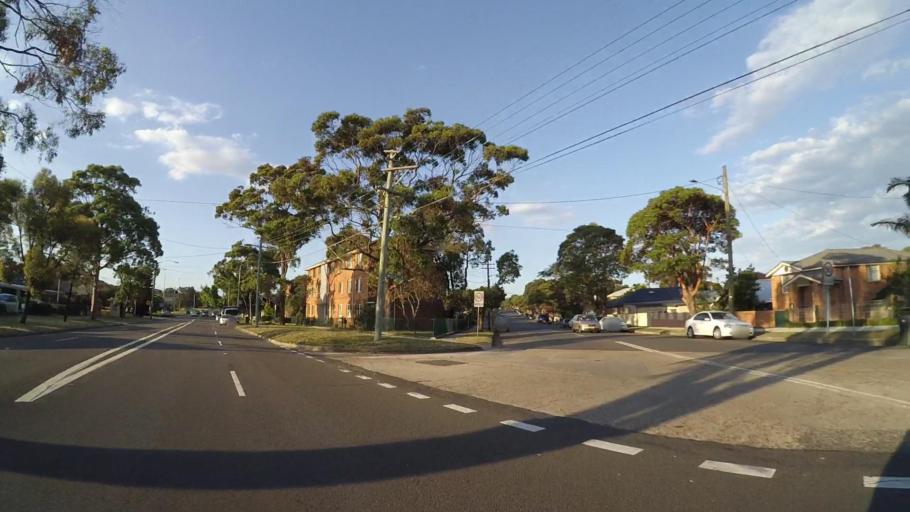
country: AU
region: New South Wales
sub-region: Randwick
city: Daceyville
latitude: -33.9329
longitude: 151.2302
